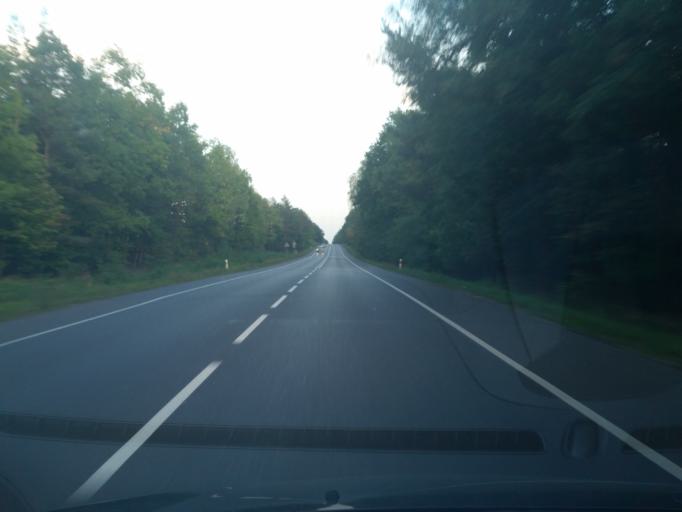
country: PL
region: Masovian Voivodeship
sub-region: Powiat warszawski zachodni
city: Kielpin
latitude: 52.3921
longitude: 20.8716
